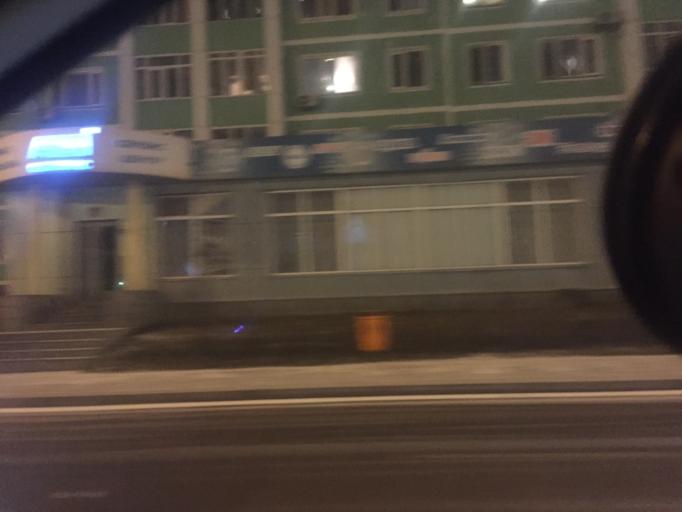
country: KZ
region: Astana Qalasy
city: Astana
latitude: 51.1683
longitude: 71.4084
